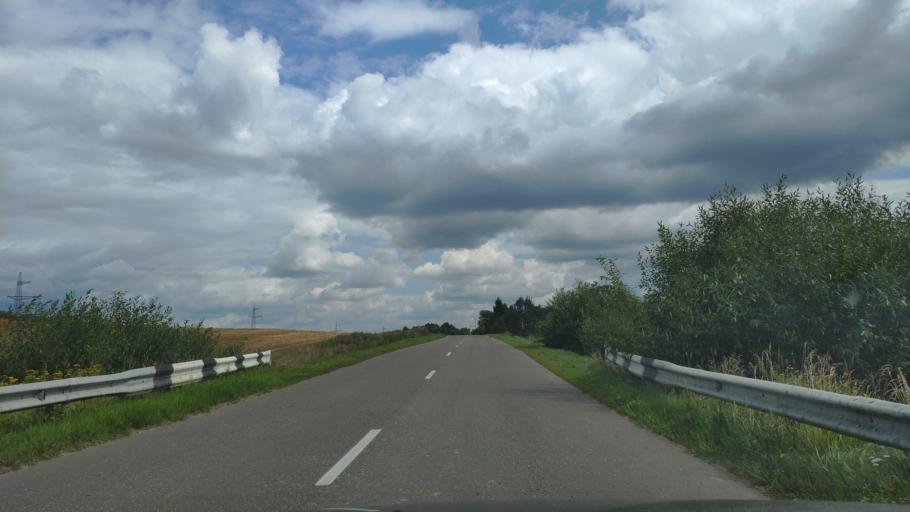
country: BY
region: Minsk
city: Khatsyezhyna
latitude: 53.8705
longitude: 27.3123
